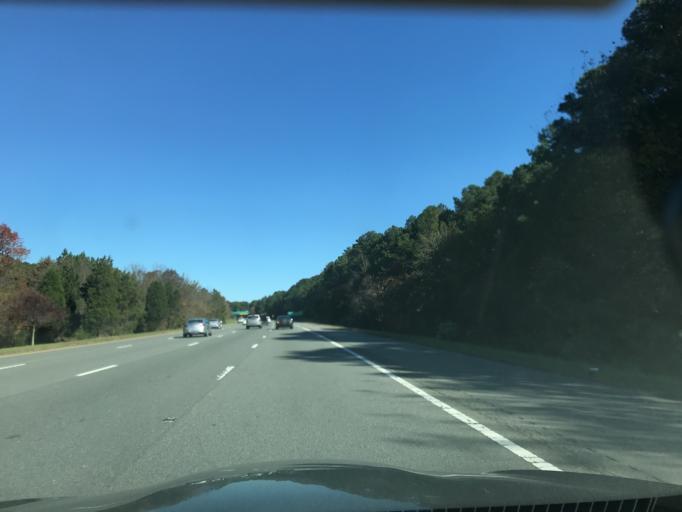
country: US
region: North Carolina
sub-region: Durham County
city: Durham
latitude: 35.9065
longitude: -78.8689
